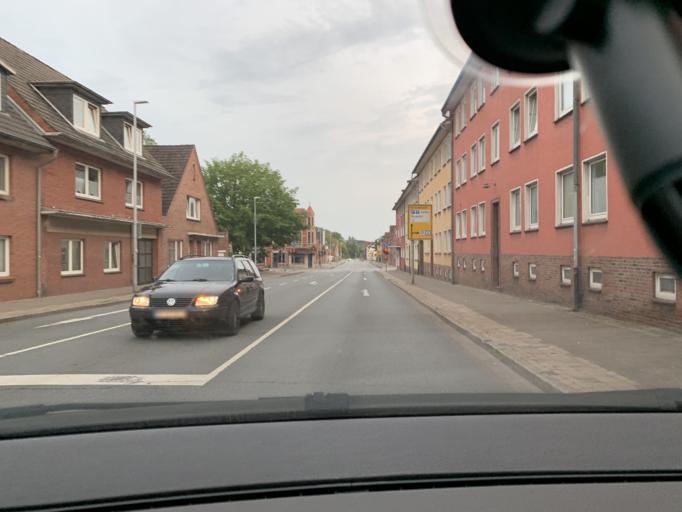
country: DE
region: Schleswig-Holstein
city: Husum
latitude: 54.4792
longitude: 9.0564
